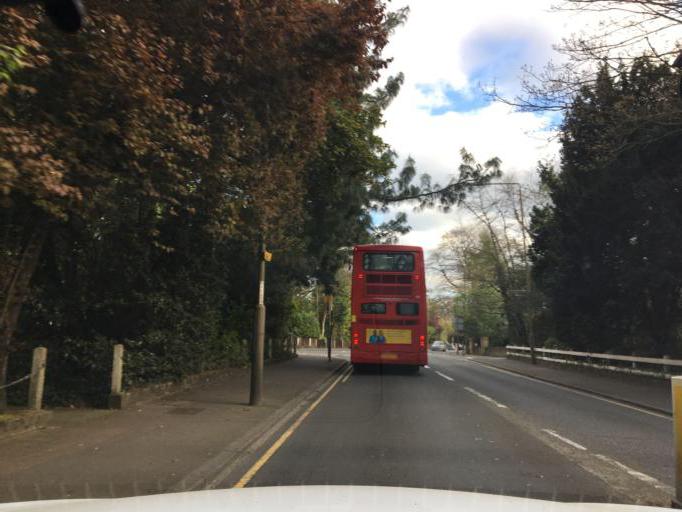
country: GB
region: England
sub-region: Greater London
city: Chislehurst
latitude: 51.4485
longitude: 0.0521
